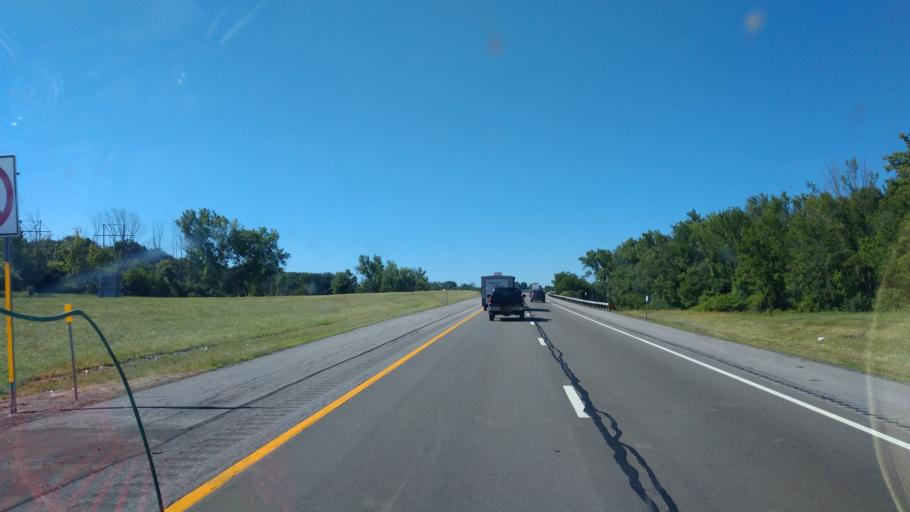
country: US
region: New York
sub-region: Erie County
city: Blasdell
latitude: 42.7706
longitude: -78.8175
